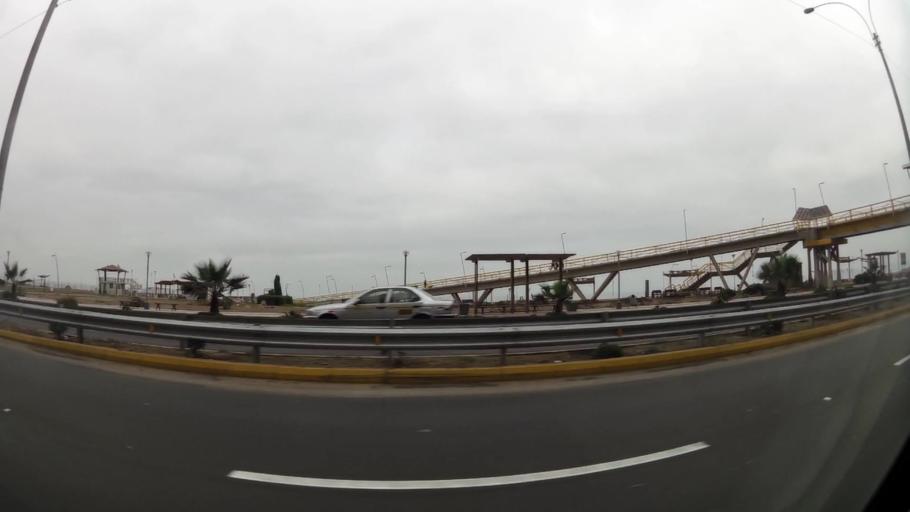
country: PE
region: Lima
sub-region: Lima
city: San Isidro
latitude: -12.0951
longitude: -77.0783
